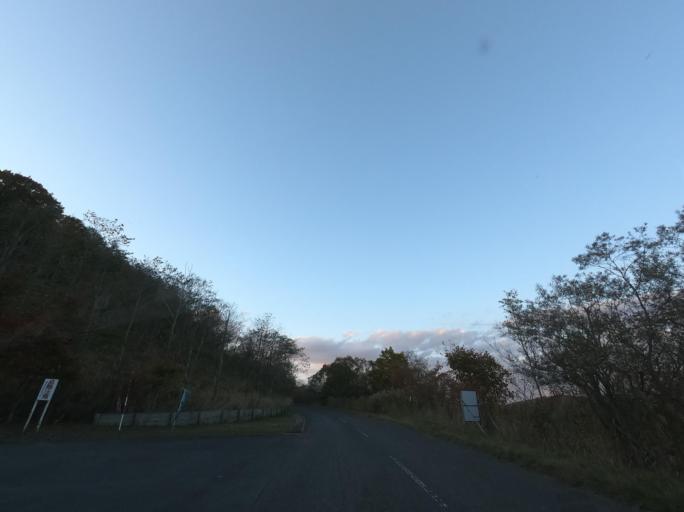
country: JP
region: Hokkaido
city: Kushiro
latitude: 43.1912
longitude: 144.4662
